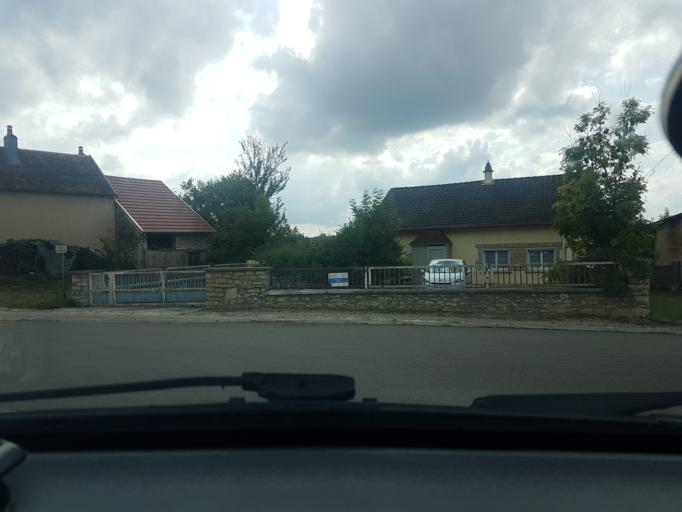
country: FR
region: Franche-Comte
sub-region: Departement du Doubs
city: Roulans
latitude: 47.4172
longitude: 6.2452
